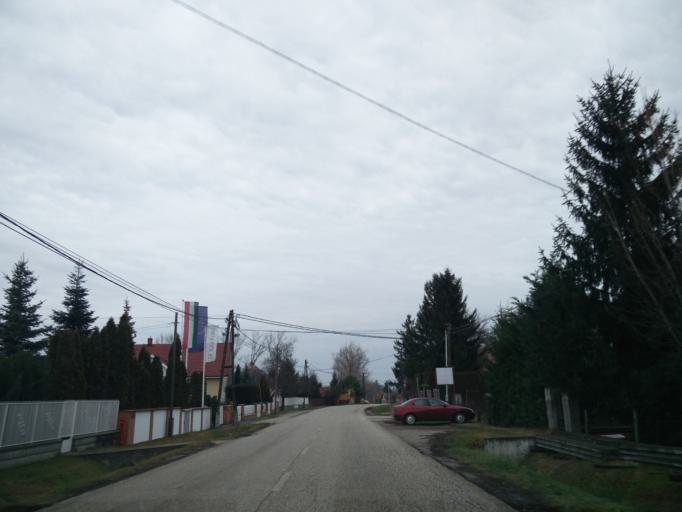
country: HU
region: Pest
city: Koka
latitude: 47.4788
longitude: 19.5706
